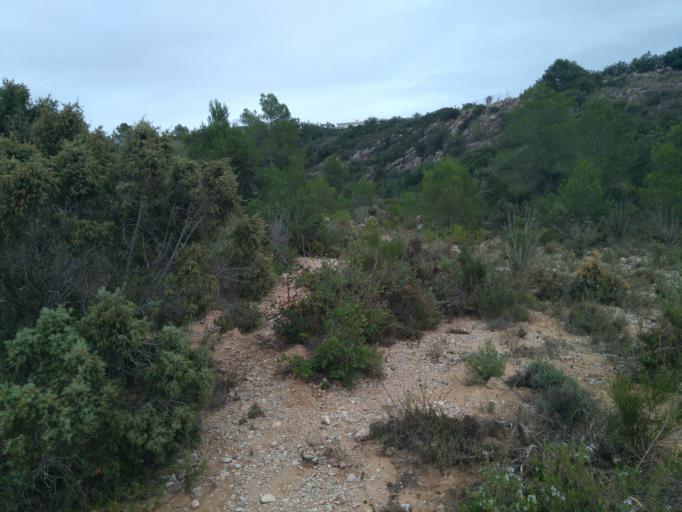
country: ES
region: Valencia
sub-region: Provincia de Valencia
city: Benimodo
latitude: 39.1966
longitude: -0.5747
